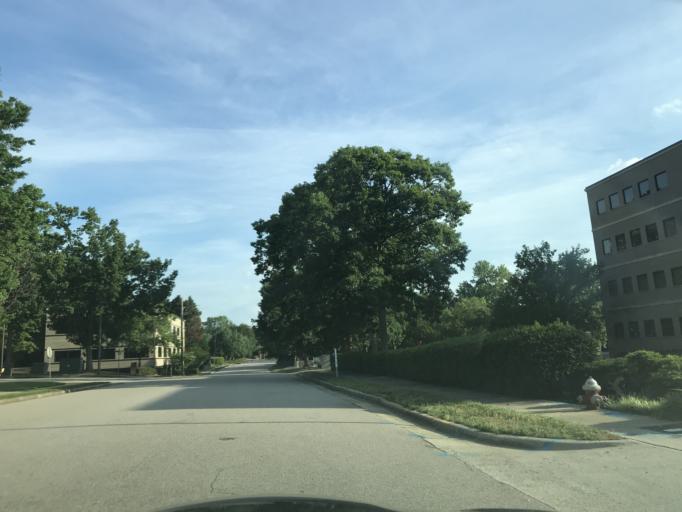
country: US
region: North Carolina
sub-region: Wake County
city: West Raleigh
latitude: 35.8149
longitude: -78.7079
